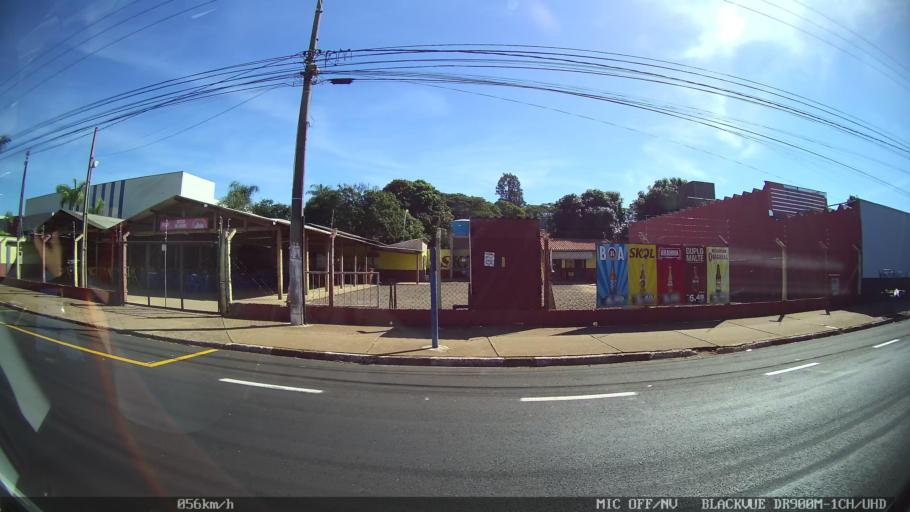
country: BR
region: Sao Paulo
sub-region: Franca
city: Franca
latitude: -20.5452
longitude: -47.4241
